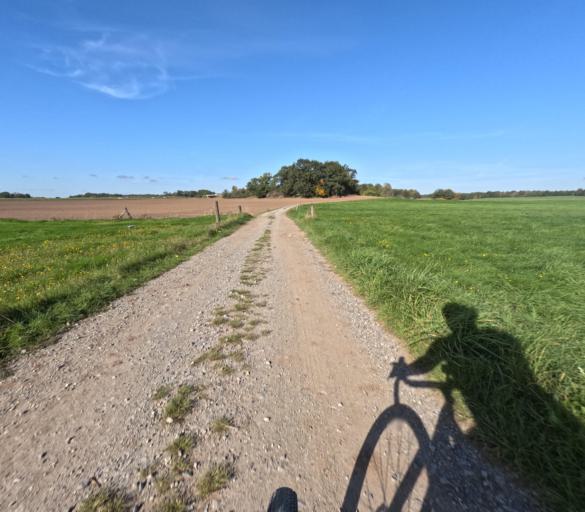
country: DE
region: Saxony
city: Radeburg
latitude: 51.1704
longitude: 13.7556
